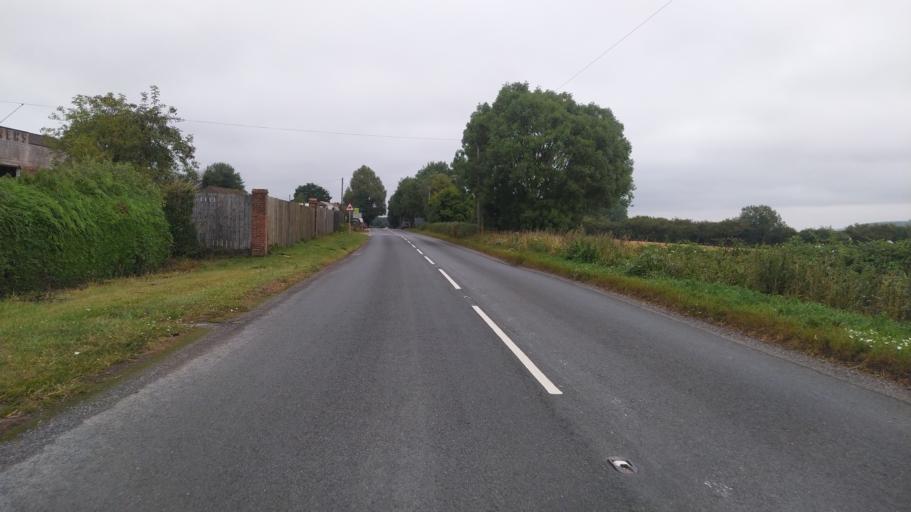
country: GB
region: England
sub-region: Wiltshire
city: Ansty
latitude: 51.0450
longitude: -2.0347
